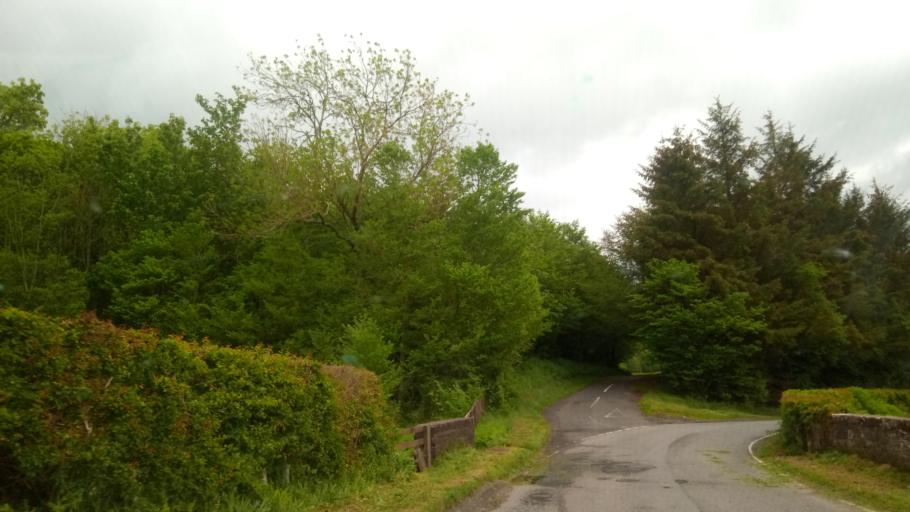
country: GB
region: Scotland
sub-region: The Scottish Borders
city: Hawick
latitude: 55.4750
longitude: -2.7120
